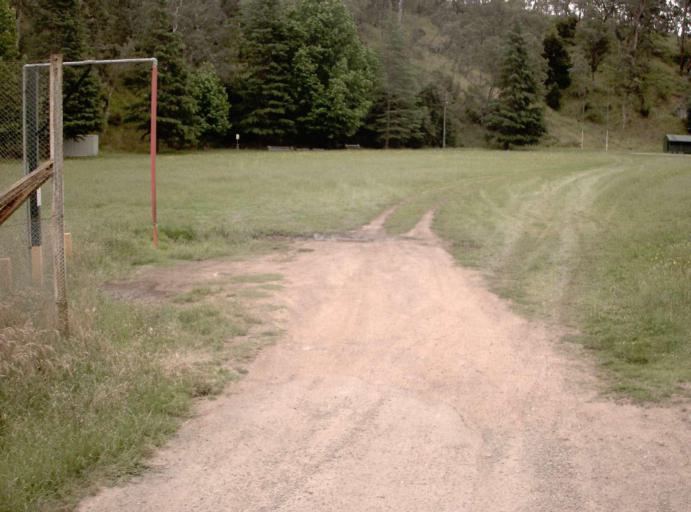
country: AU
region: Victoria
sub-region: East Gippsland
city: Bairnsdale
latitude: -37.4570
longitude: 147.2510
